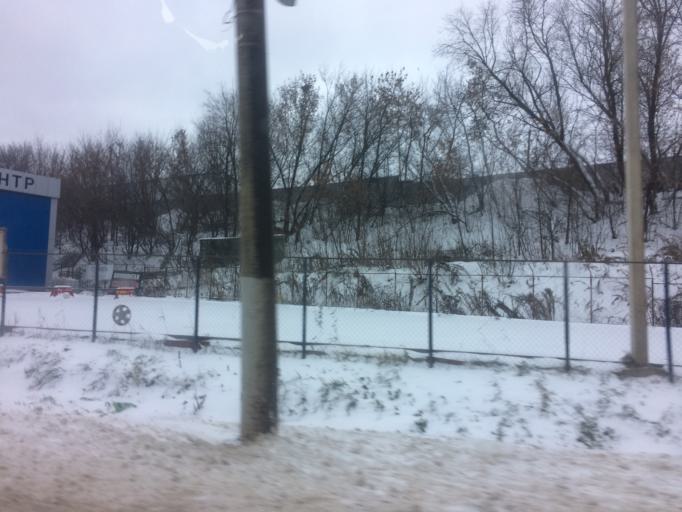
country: RU
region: Tula
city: Tula
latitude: 54.1691
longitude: 37.6346
